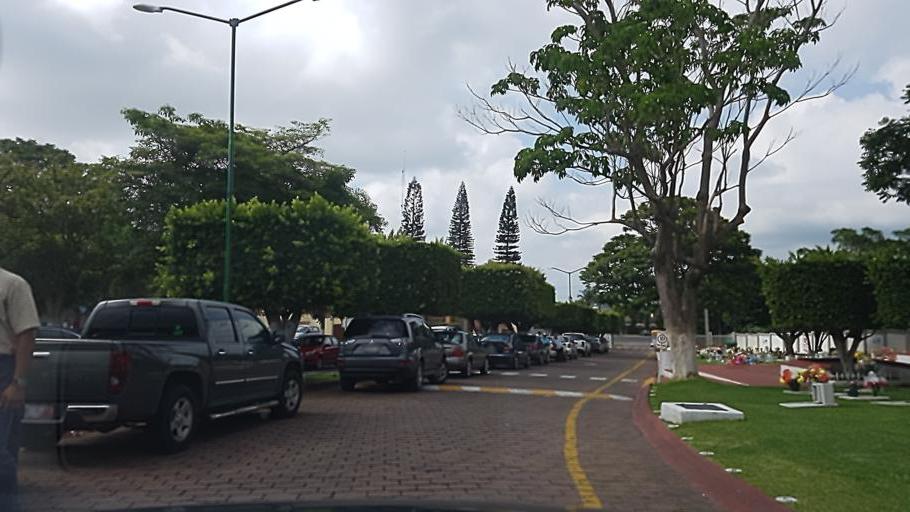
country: MX
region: Nayarit
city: Tepic
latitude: 21.5213
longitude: -104.9297
